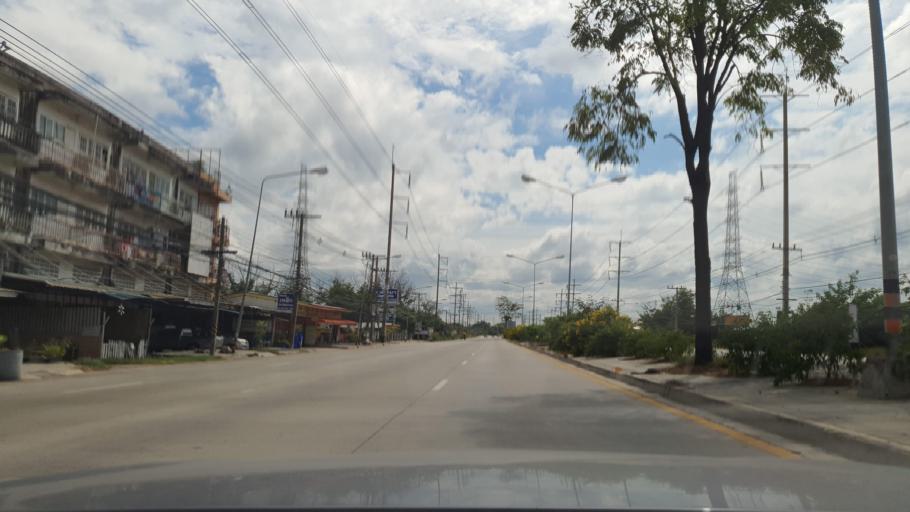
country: TH
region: Chachoengsao
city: Bang Pakong
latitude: 13.5243
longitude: 100.9920
